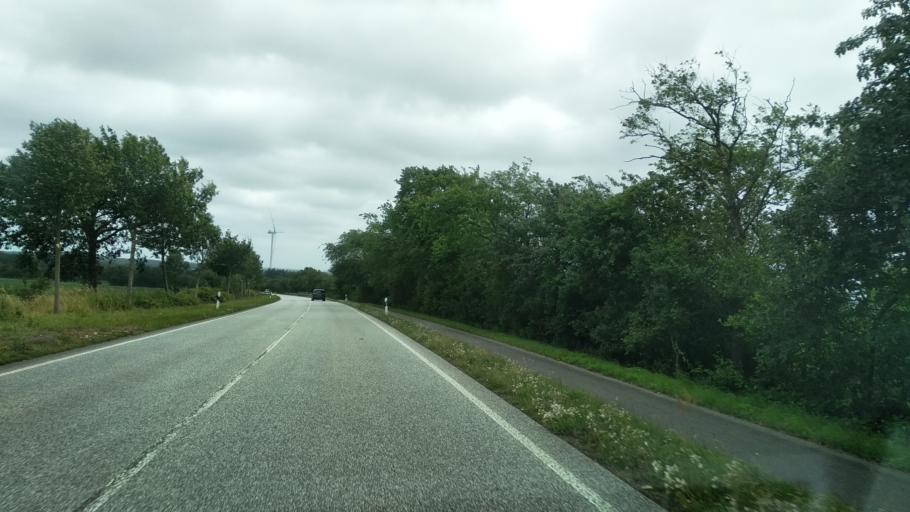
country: DE
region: Schleswig-Holstein
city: Tarp
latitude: 54.6572
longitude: 9.4414
